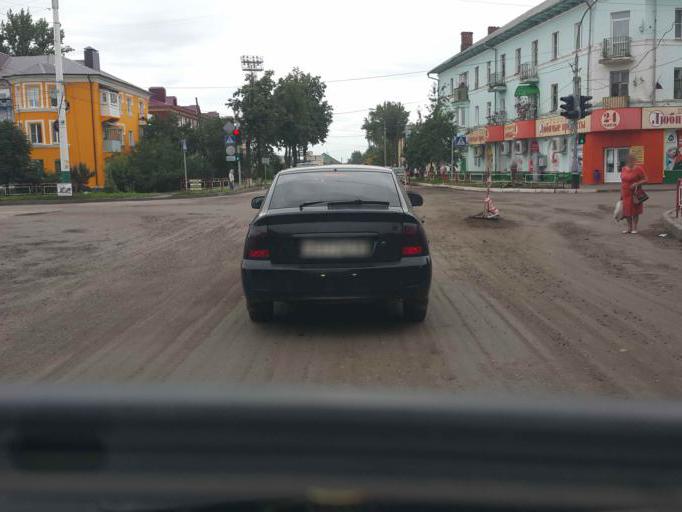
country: RU
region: Tambov
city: Michurinsk
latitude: 52.8971
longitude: 40.5035
